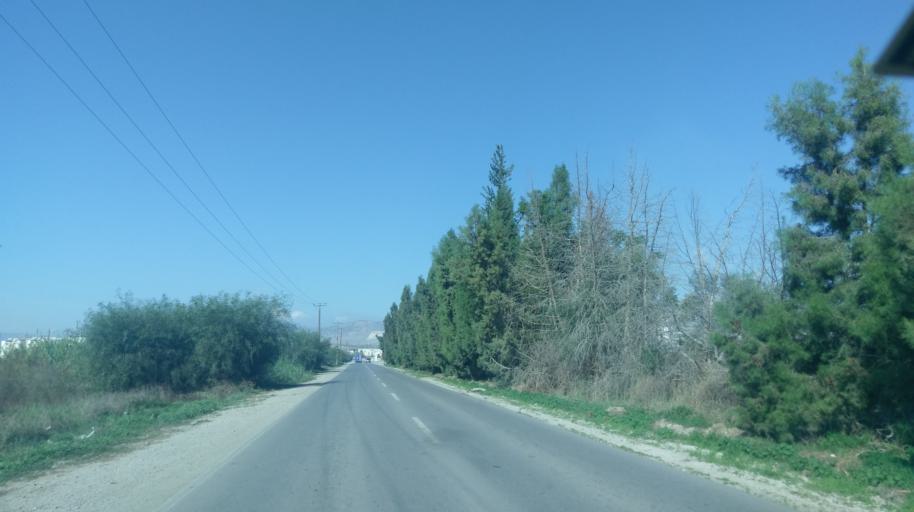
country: CY
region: Lefkosia
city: Nicosia
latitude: 35.2110
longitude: 33.4270
